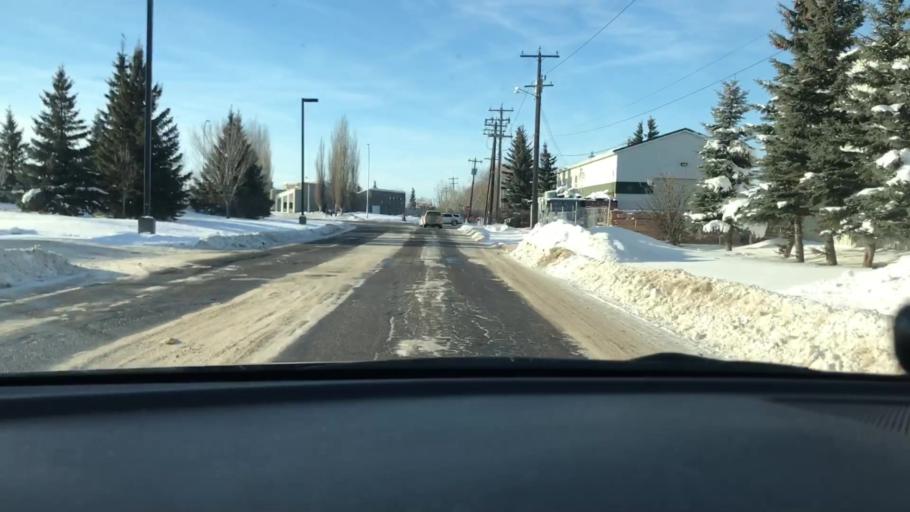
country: CA
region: Alberta
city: Edmonton
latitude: 53.4540
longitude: -113.4774
